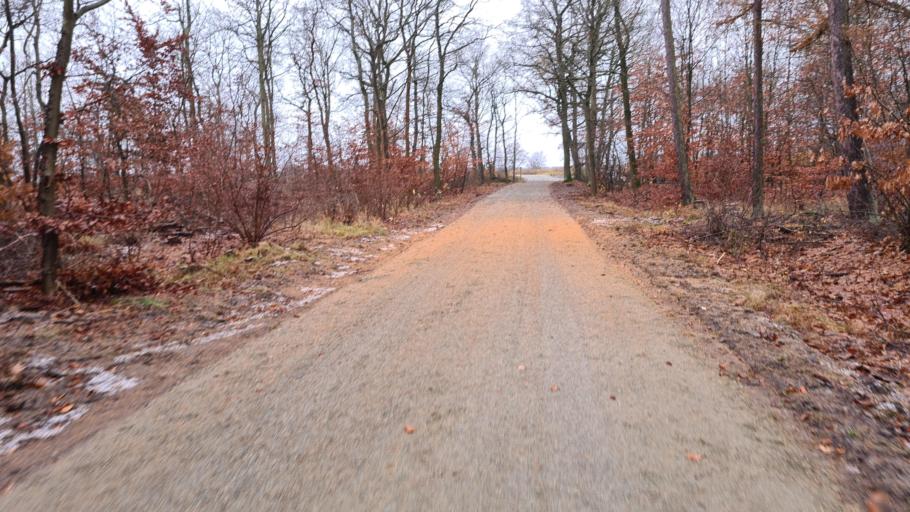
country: DE
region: Brandenburg
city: Finsterwalde
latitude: 51.6231
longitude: 13.6810
